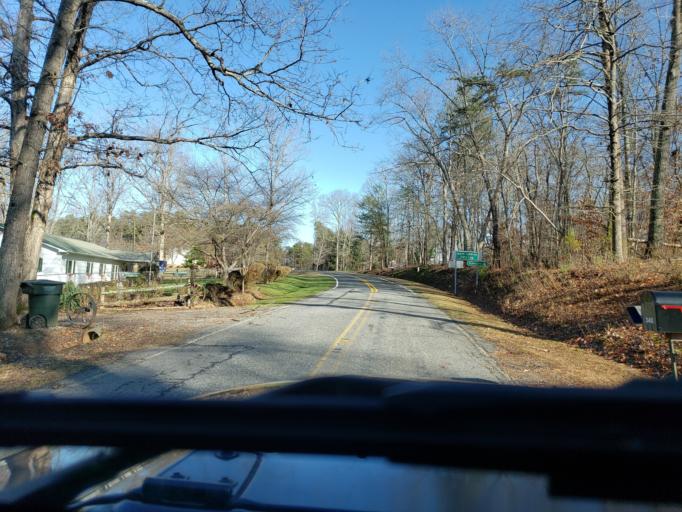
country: US
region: North Carolina
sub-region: Cleveland County
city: White Plains
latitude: 35.1671
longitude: -81.4107
